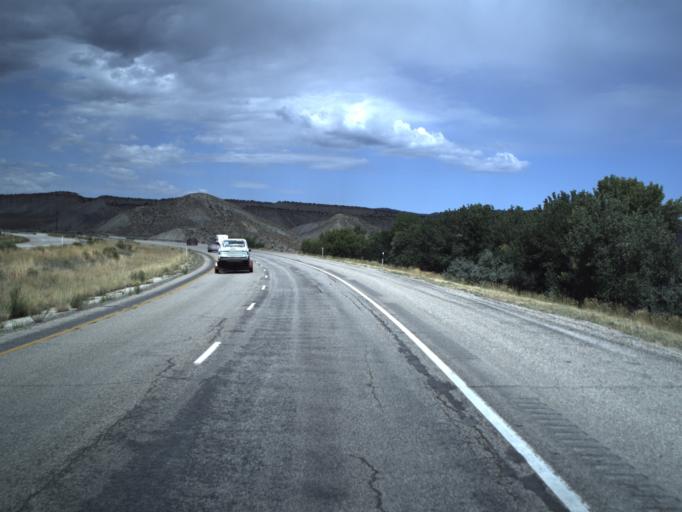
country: US
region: Utah
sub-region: Carbon County
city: Carbonville
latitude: 39.6154
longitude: -110.8401
